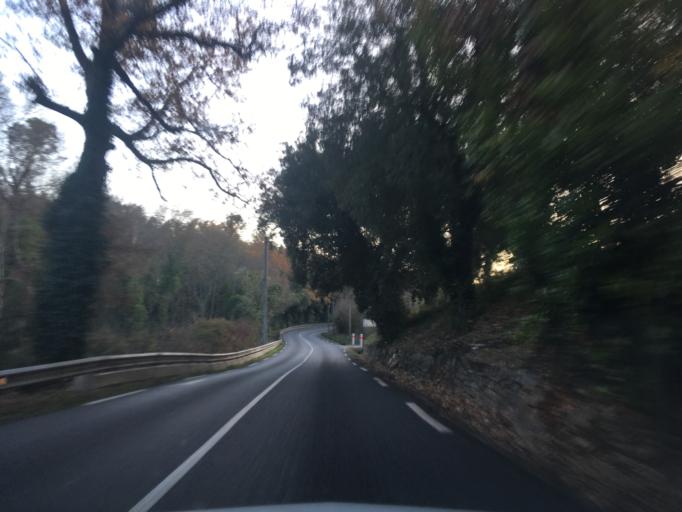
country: FR
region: Provence-Alpes-Cote d'Azur
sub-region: Departement des Alpes-Maritimes
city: Le Tignet
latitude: 43.6154
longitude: 6.8213
